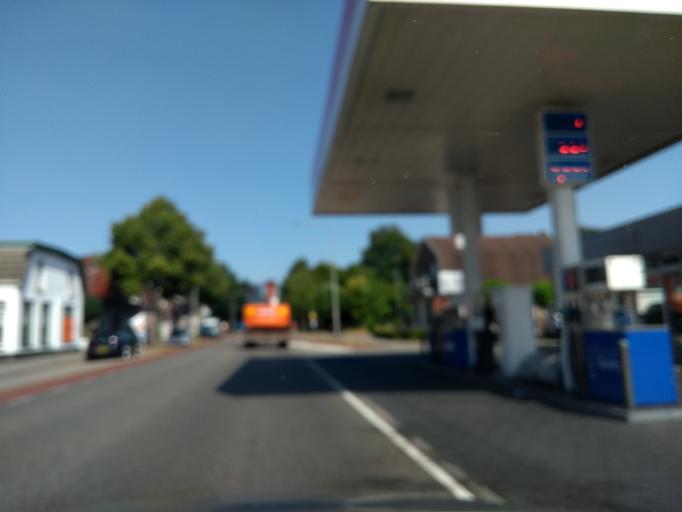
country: NL
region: Overijssel
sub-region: Gemeente Twenterand
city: Vroomshoop
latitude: 52.4616
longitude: 6.5747
